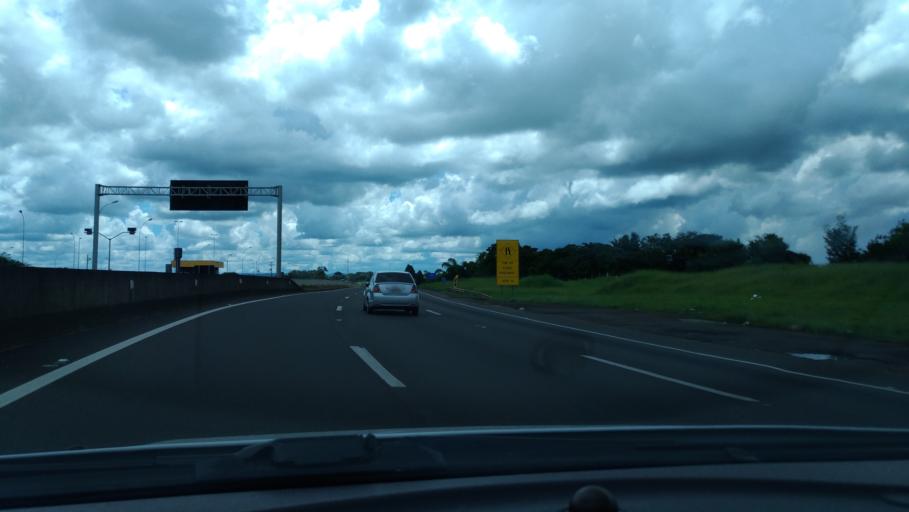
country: BR
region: Sao Paulo
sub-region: Itirapina
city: Itirapina
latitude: -22.2688
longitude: -47.7040
